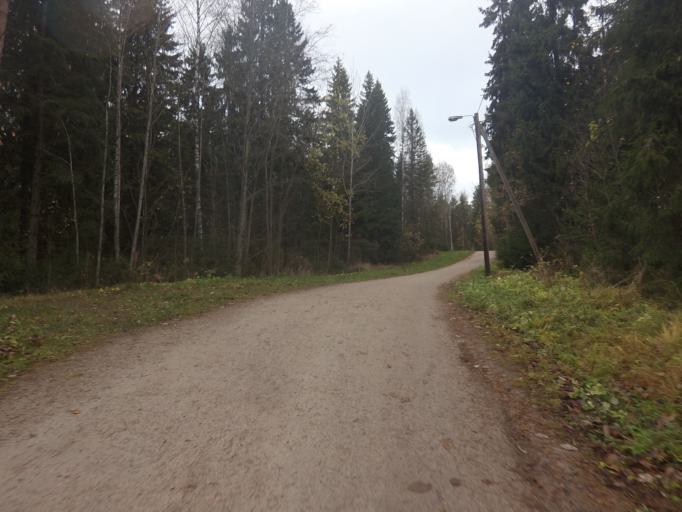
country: FI
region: Uusimaa
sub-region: Helsinki
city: Espoo
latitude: 60.1913
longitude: 24.6843
